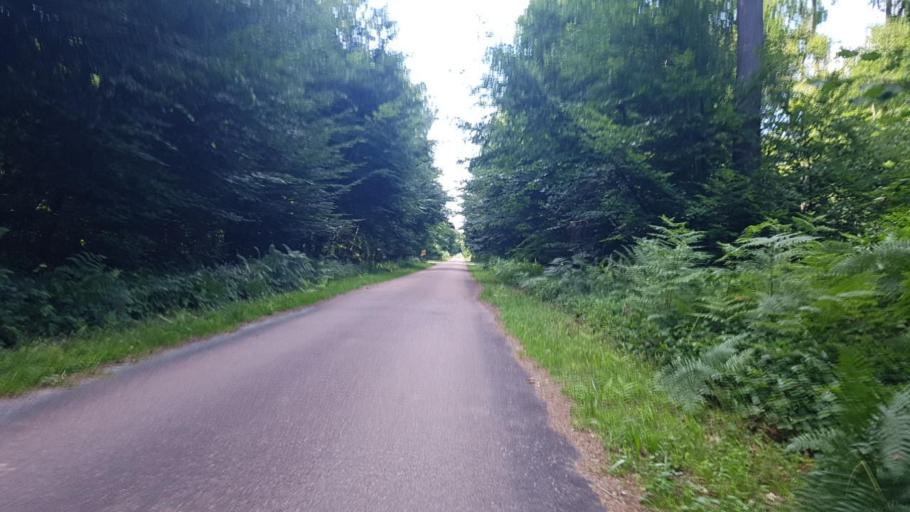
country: FR
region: Picardie
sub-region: Departement de l'Oise
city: Chamant
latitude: 49.1627
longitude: 2.6349
